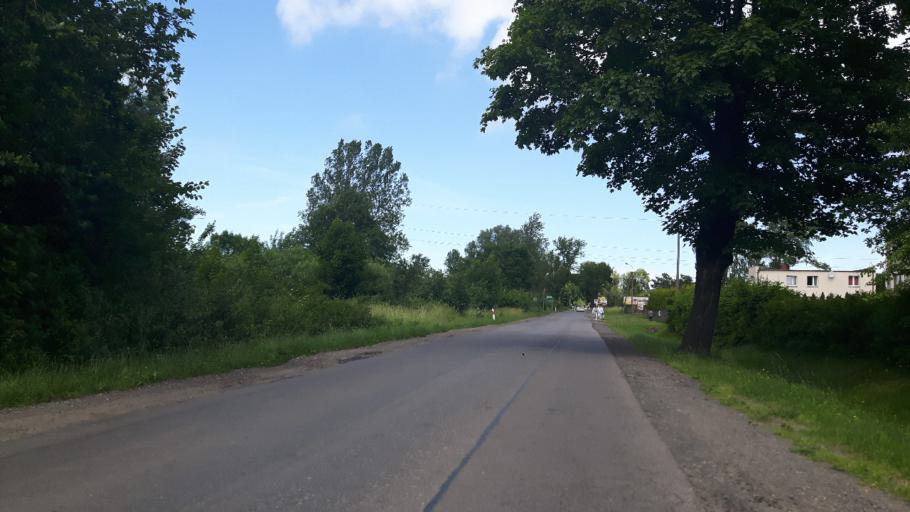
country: PL
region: Pomeranian Voivodeship
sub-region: Powiat slupski
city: Ustka
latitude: 54.5658
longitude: 16.8488
